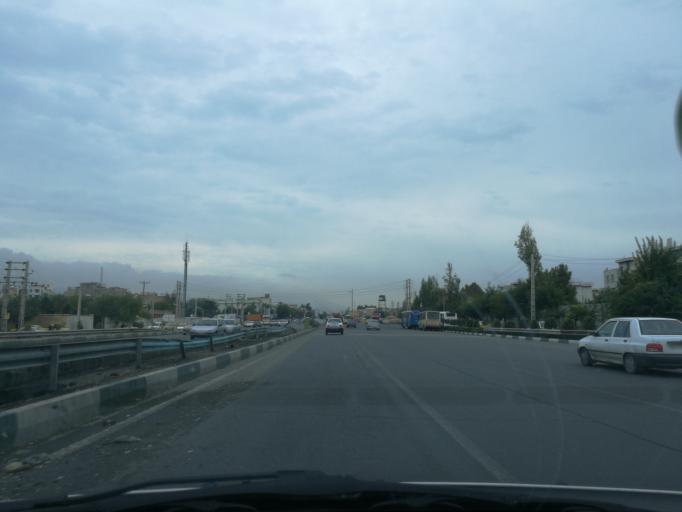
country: IR
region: Alborz
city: Karaj
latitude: 35.8482
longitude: 50.9127
